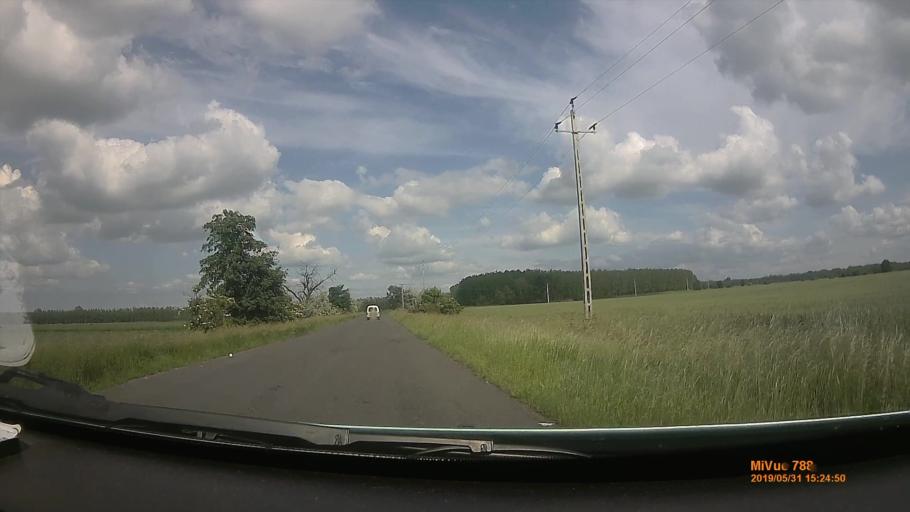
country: HU
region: Borsod-Abauj-Zemplen
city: Taktaharkany
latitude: 48.0663
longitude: 21.1592
